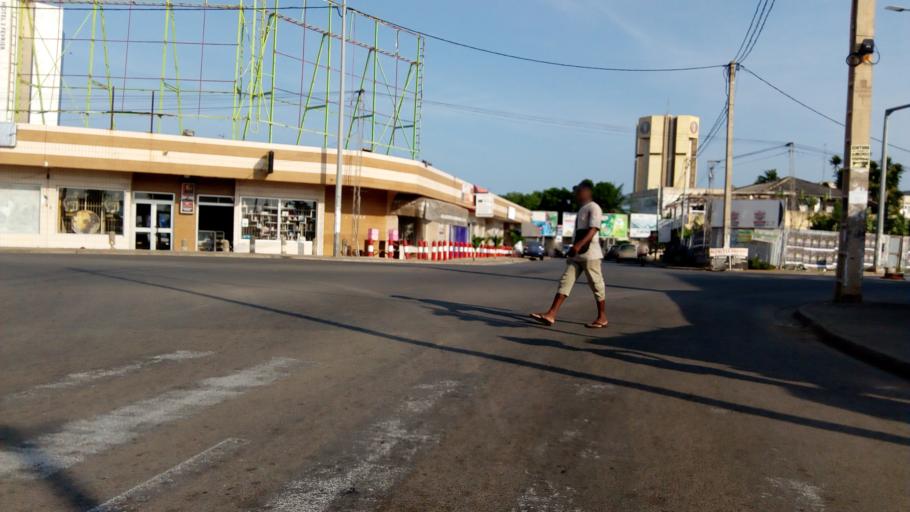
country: TG
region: Maritime
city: Lome
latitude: 6.1306
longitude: 1.2122
